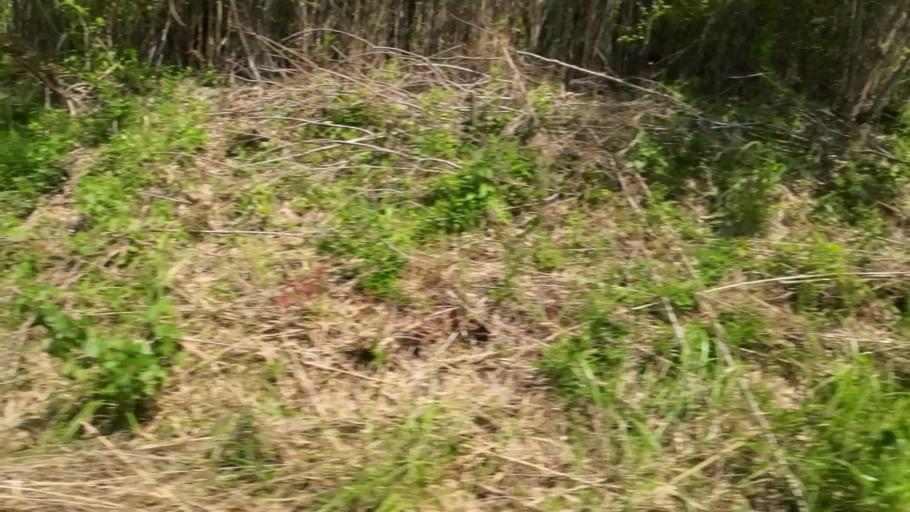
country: JP
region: Ehime
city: Saijo
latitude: 33.9224
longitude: 133.2453
